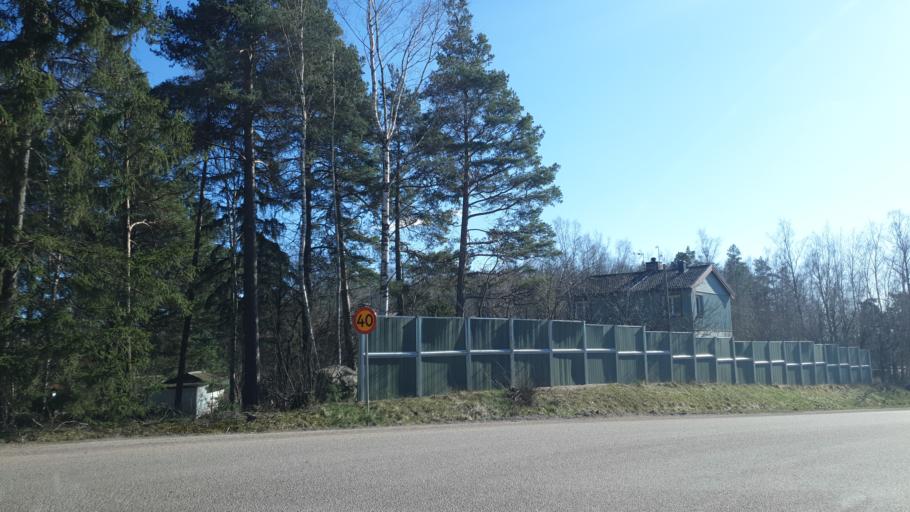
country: SE
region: Vaestmanland
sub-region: Kopings Kommun
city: Koping
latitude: 59.5007
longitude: 16.0388
